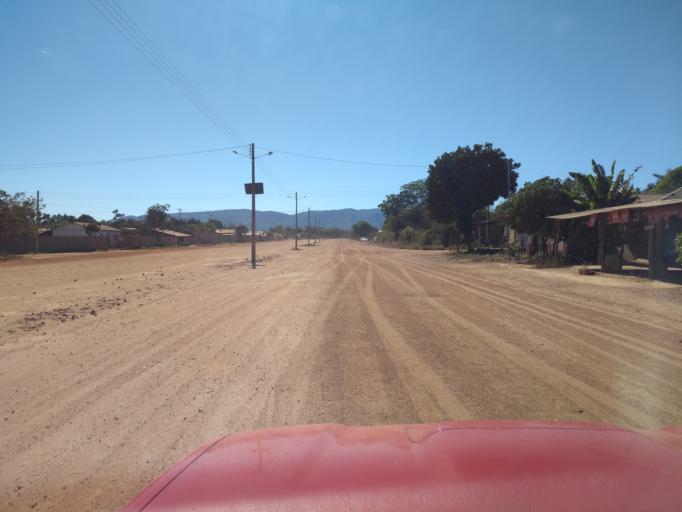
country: BR
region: Goias
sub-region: Cavalcante
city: Cavalcante
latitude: -13.7990
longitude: -47.4443
